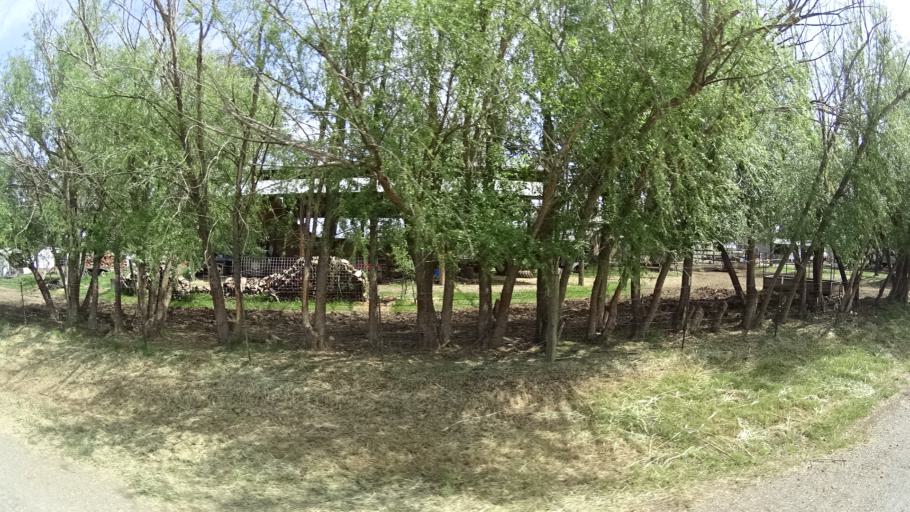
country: US
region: California
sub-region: Glenn County
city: Orland
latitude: 39.7878
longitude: -122.1597
